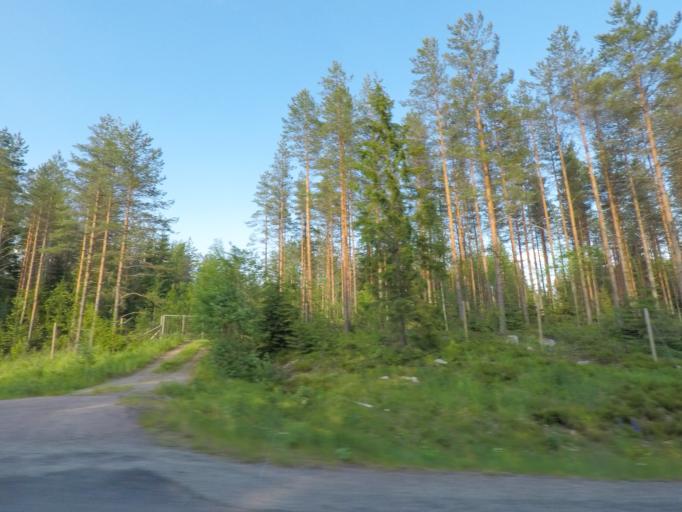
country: FI
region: Central Finland
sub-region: Jyvaeskylae
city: Toivakka
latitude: 61.9965
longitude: 26.0567
